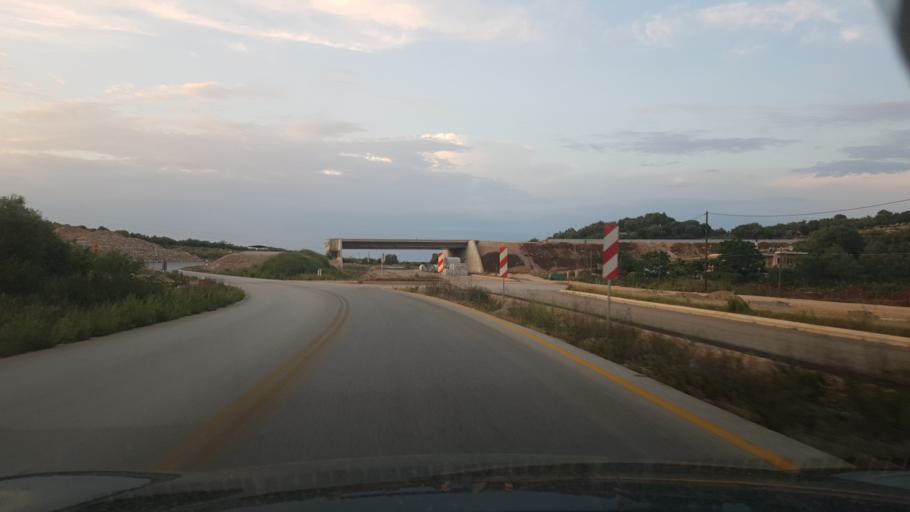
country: GR
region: West Greece
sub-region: Nomos Aitolias kai Akarnanias
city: Vonitsa
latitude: 38.8990
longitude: 20.8746
